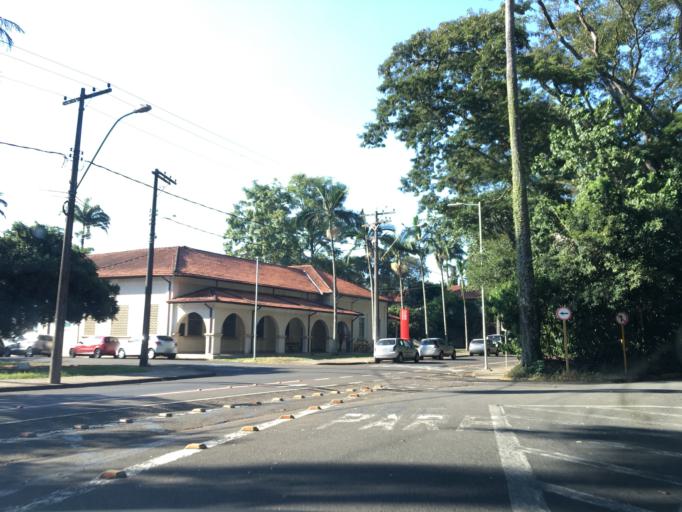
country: BR
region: Sao Paulo
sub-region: Piracicaba
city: Piracicaba
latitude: -22.7106
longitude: -47.6345
